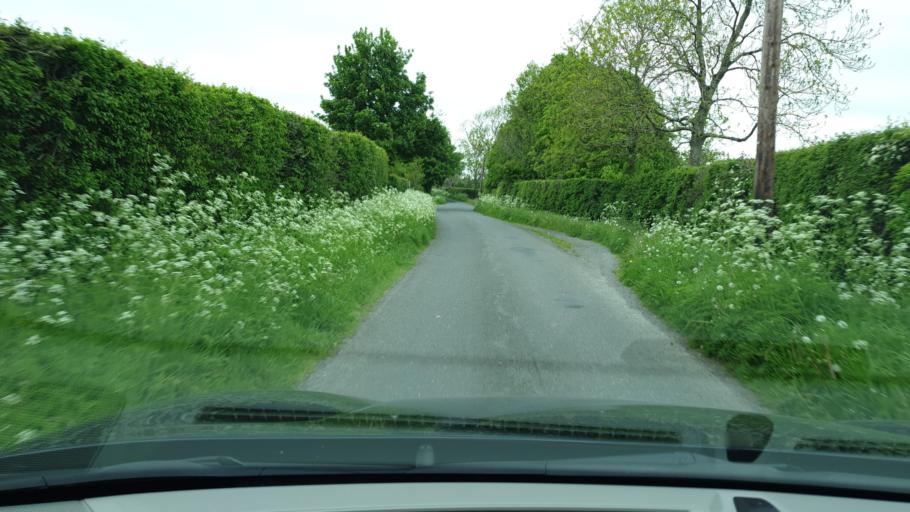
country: IE
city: Confey
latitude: 53.4155
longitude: -6.5325
